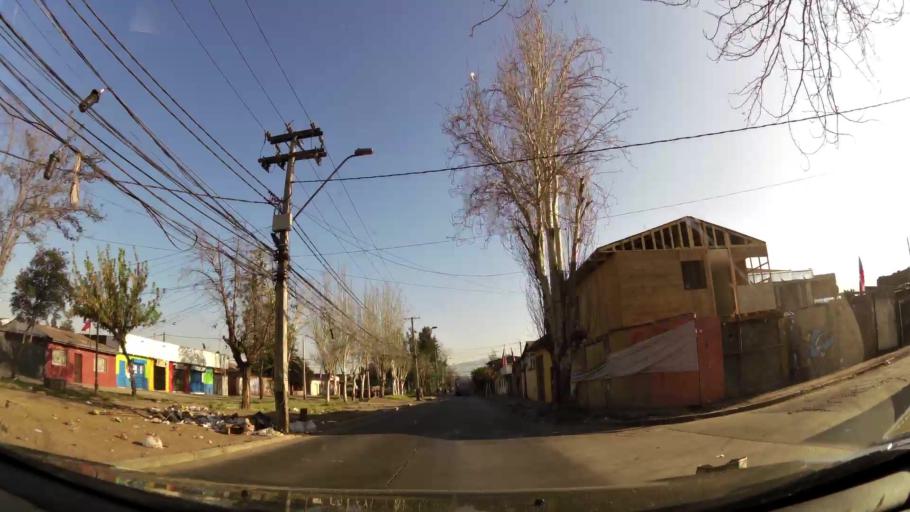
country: CL
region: Santiago Metropolitan
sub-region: Provincia de Santiago
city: Santiago
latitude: -33.3853
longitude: -70.6717
